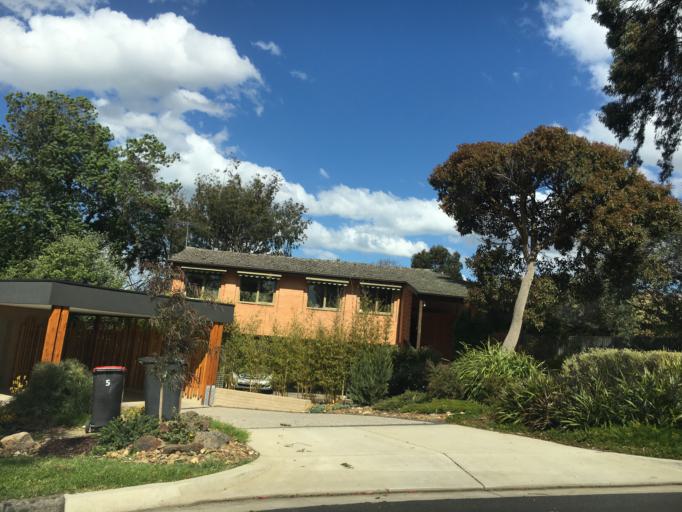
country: AU
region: Victoria
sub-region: Monash
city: Mulgrave
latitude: -37.8949
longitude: 145.1793
